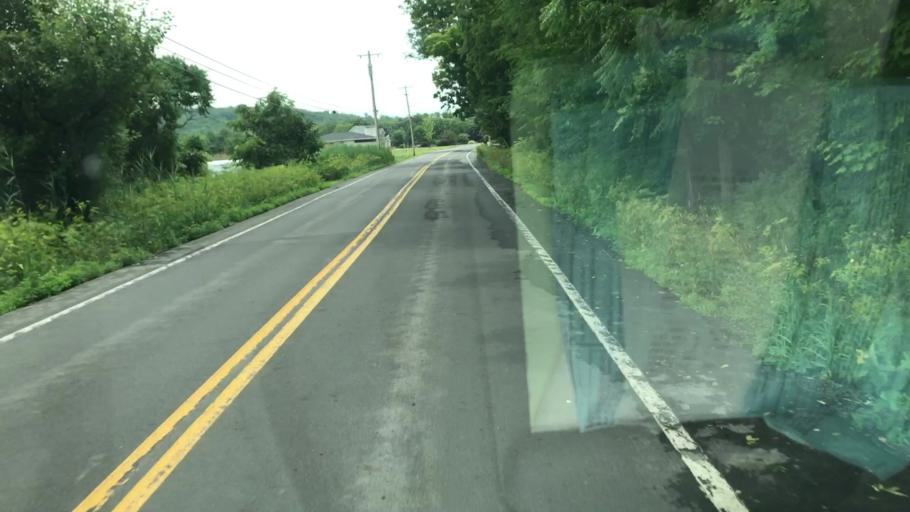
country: US
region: New York
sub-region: Onondaga County
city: Manlius
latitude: 42.9702
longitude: -75.9880
